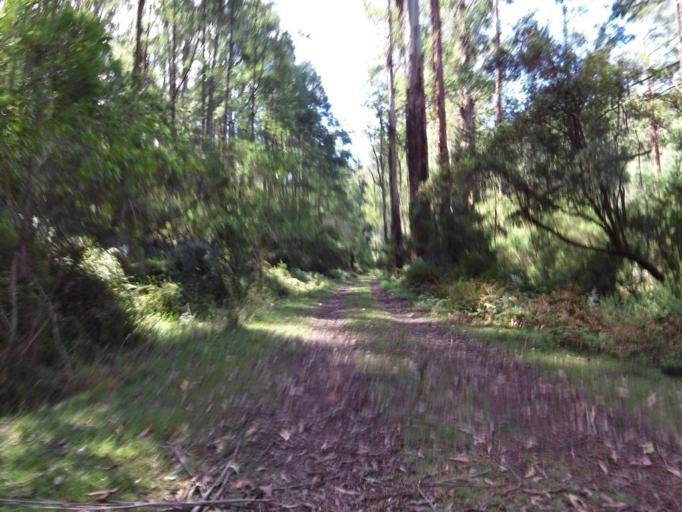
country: AU
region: Victoria
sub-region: Yarra Ranges
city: Millgrove
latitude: -37.6858
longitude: 145.8082
